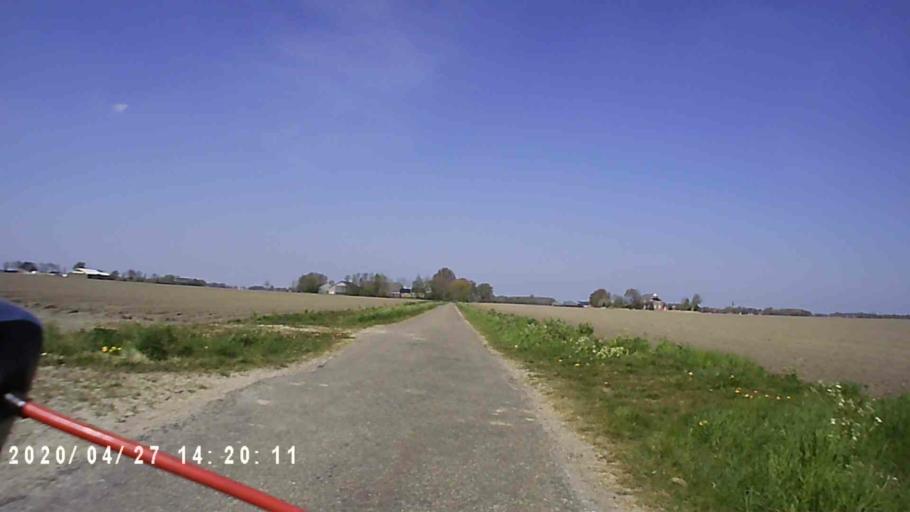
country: NL
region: Groningen
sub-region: Gemeente De Marne
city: Ulrum
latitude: 53.3704
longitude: 6.3836
